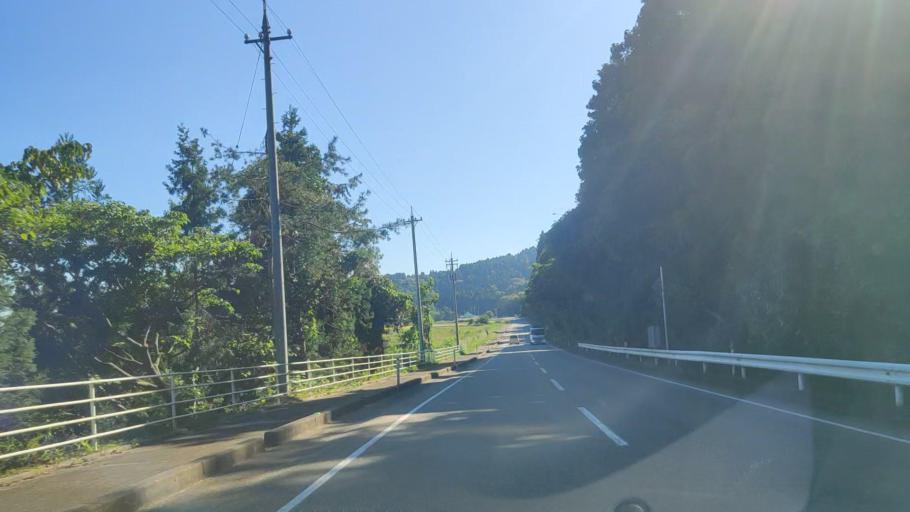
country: JP
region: Ishikawa
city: Nanao
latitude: 37.3922
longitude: 137.2342
